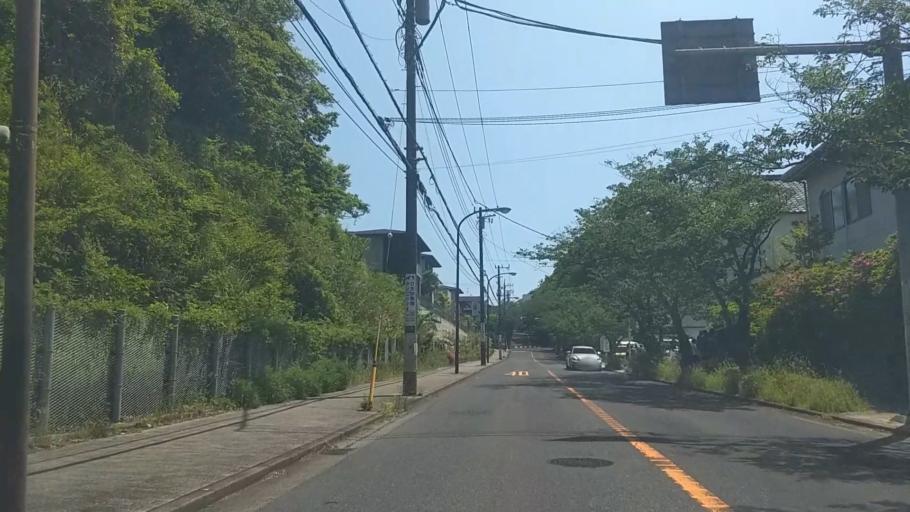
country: JP
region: Kanagawa
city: Zushi
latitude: 35.3190
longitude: 139.5774
